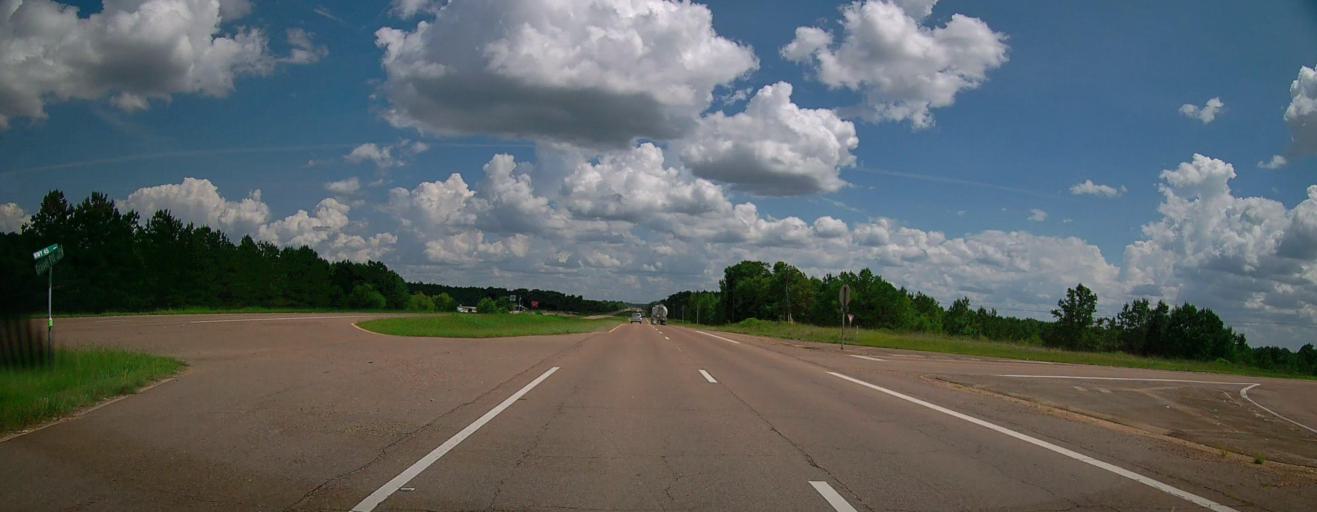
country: US
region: Mississippi
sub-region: Lowndes County
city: Columbus Air Force Base
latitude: 33.6890
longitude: -88.4379
